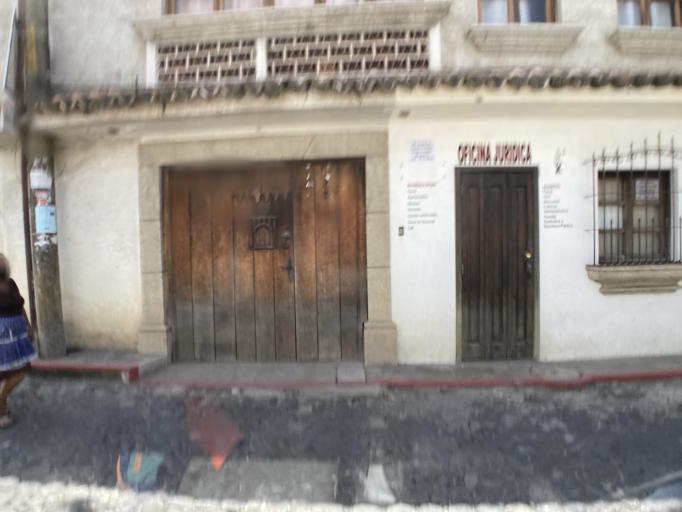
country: GT
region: Sacatepequez
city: Ciudad Vieja
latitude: 14.5292
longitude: -90.7426
